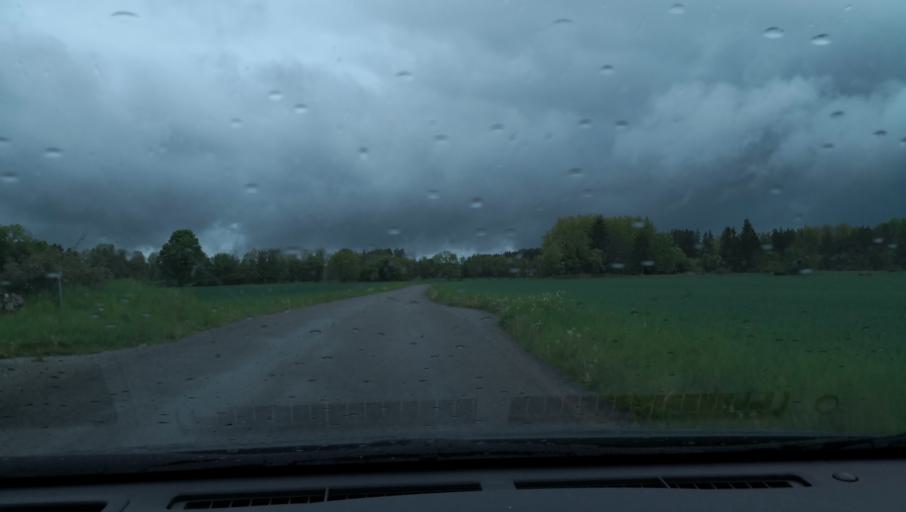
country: SE
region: Uppsala
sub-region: Enkopings Kommun
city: Orsundsbro
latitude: 59.8053
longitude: 17.3781
